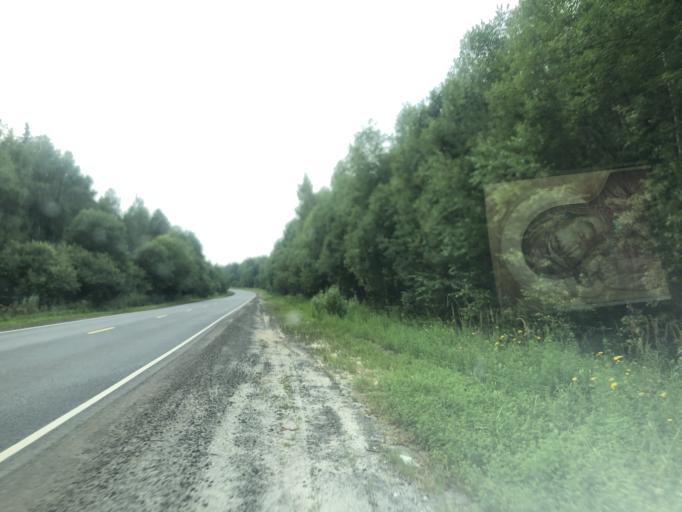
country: RU
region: Ivanovo
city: Verkhniy Landekh
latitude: 56.7800
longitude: 42.3708
